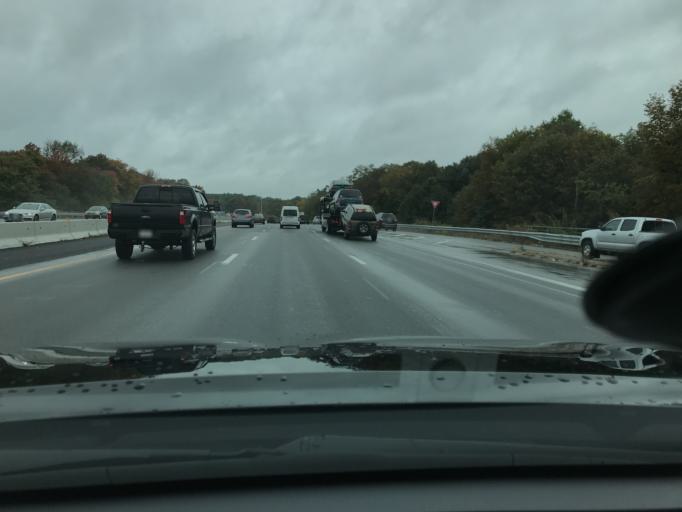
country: US
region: Massachusetts
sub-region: Middlesex County
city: Wakefield
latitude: 42.5260
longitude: -71.0658
